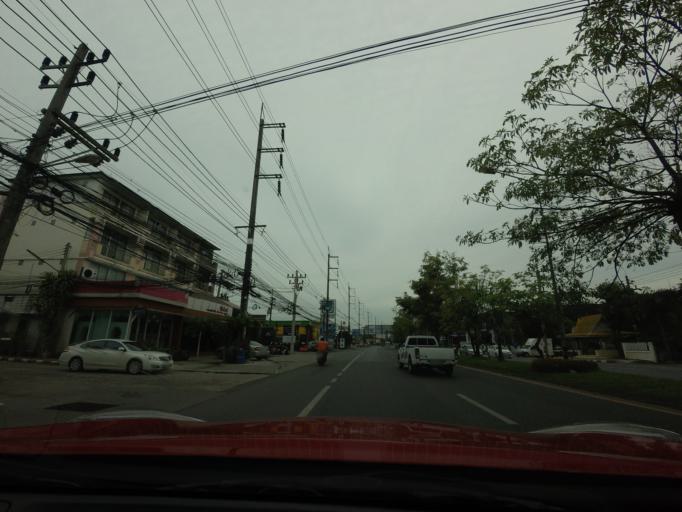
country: TH
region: Songkhla
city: Hat Yai
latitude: 6.9808
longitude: 100.4794
